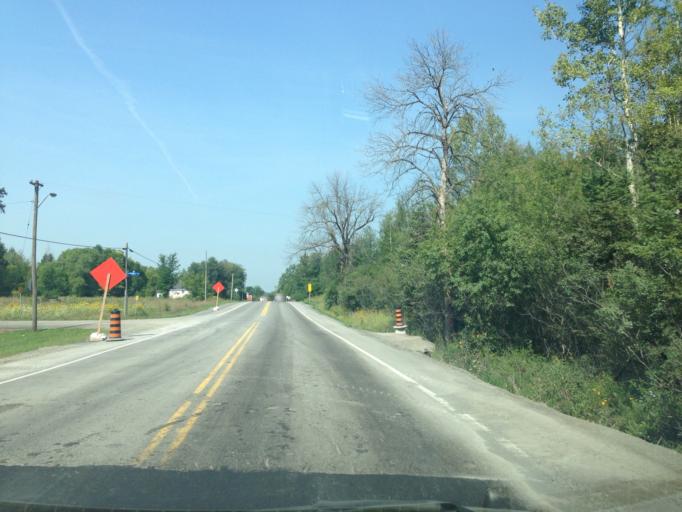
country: CA
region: Ontario
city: Ottawa
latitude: 45.4200
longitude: -75.5692
